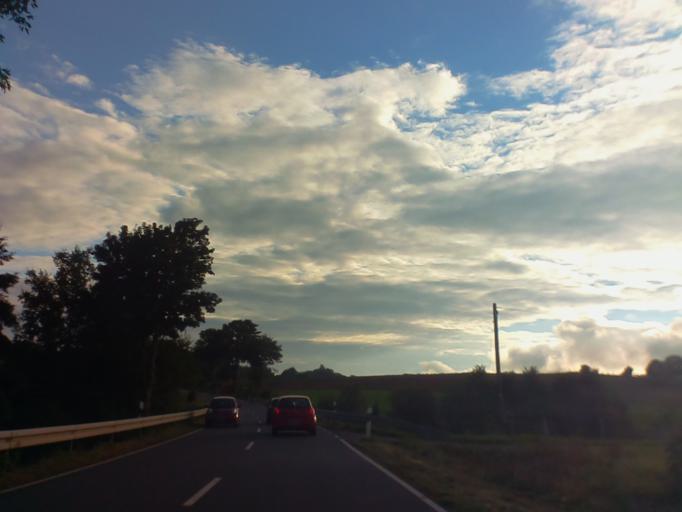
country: DE
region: Hesse
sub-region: Regierungsbezirk Darmstadt
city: Frankisch-Crumbach
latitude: 49.7310
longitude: 8.8489
